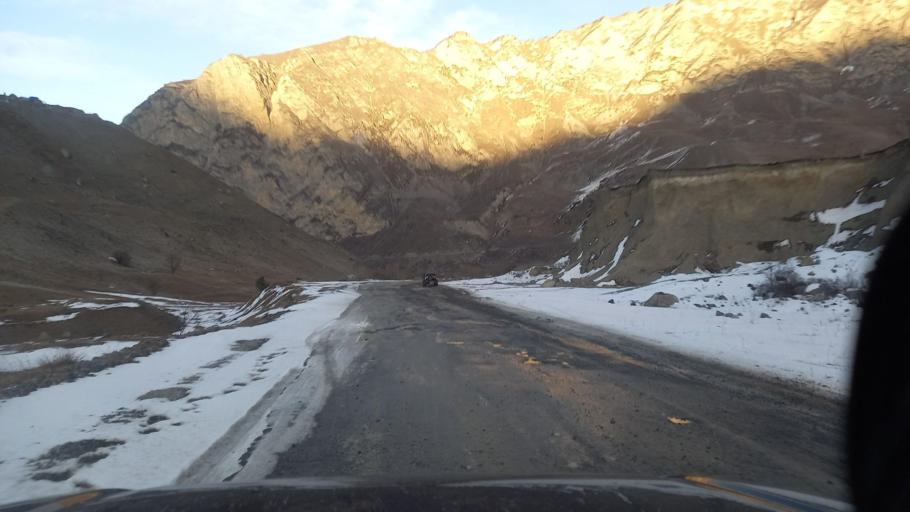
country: RU
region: Ingushetiya
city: Dzhayrakh
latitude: 42.8478
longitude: 44.5166
